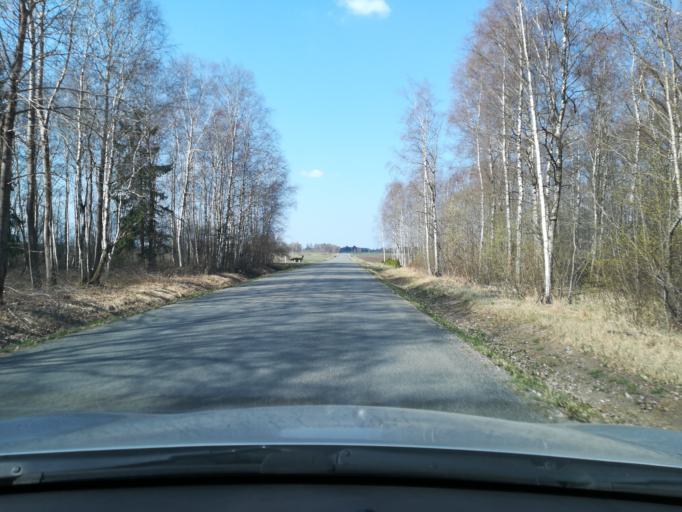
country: EE
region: Harju
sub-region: Saue linn
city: Saue
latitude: 59.3296
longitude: 24.5308
